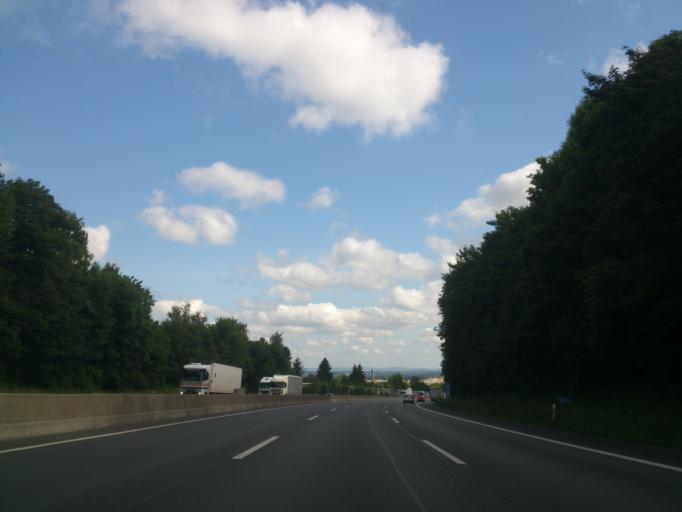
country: DE
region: North Rhine-Westphalia
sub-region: Regierungsbezirk Detmold
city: Oerlinghausen
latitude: 51.9858
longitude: 8.6152
